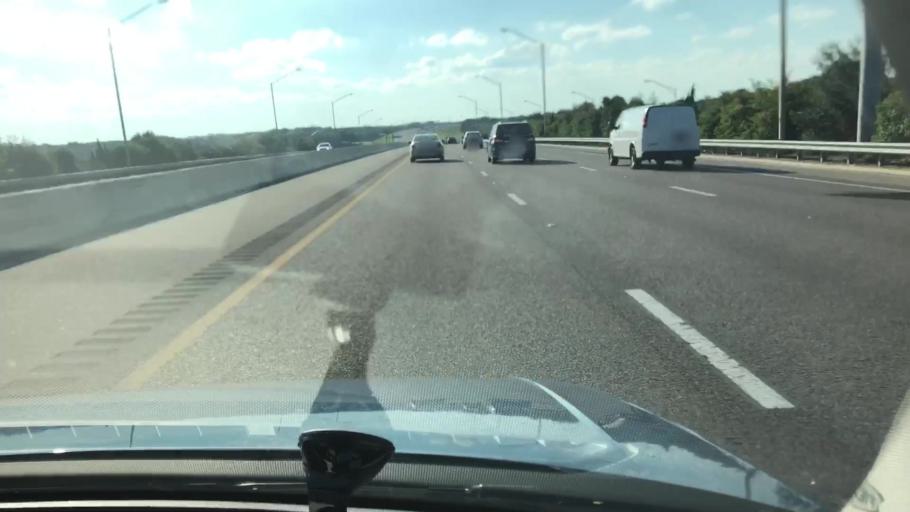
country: US
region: Florida
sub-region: Orange County
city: Clarcona
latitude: 28.6344
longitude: -81.4777
